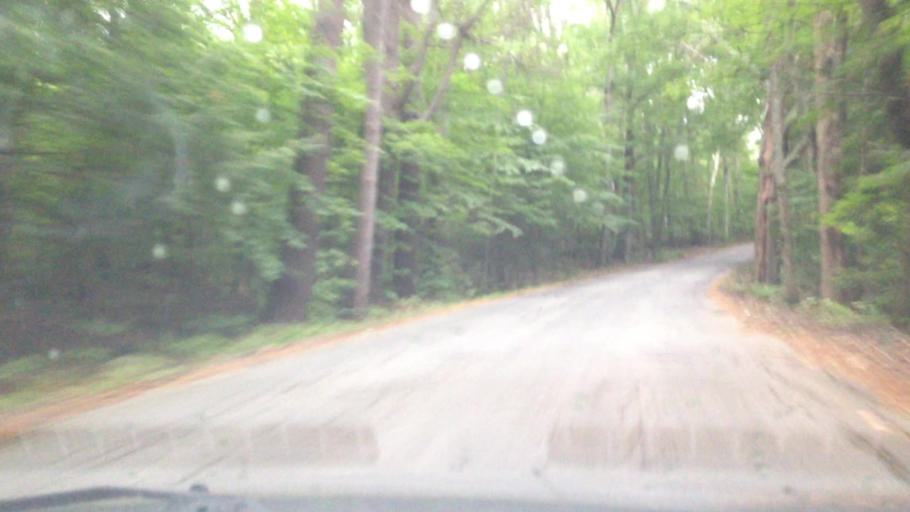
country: US
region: New Hampshire
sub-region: Cheshire County
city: Marlborough
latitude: 42.8964
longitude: -72.1964
